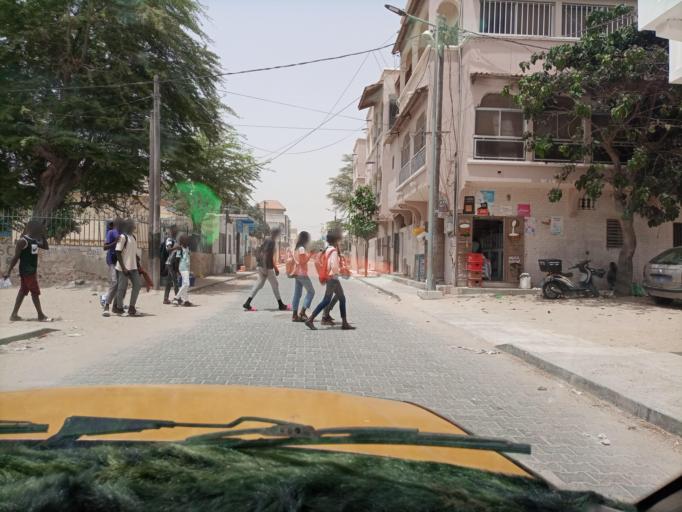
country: SN
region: Saint-Louis
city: Saint-Louis
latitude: 16.0220
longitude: -16.4901
